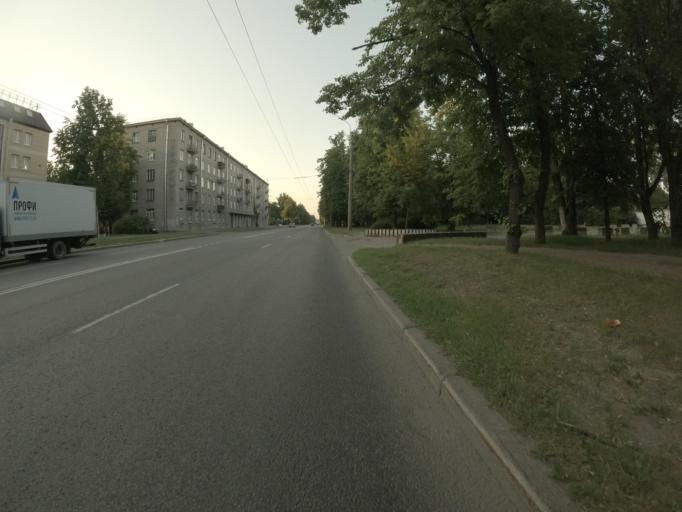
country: RU
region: St.-Petersburg
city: Avtovo
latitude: 59.8717
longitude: 30.2735
